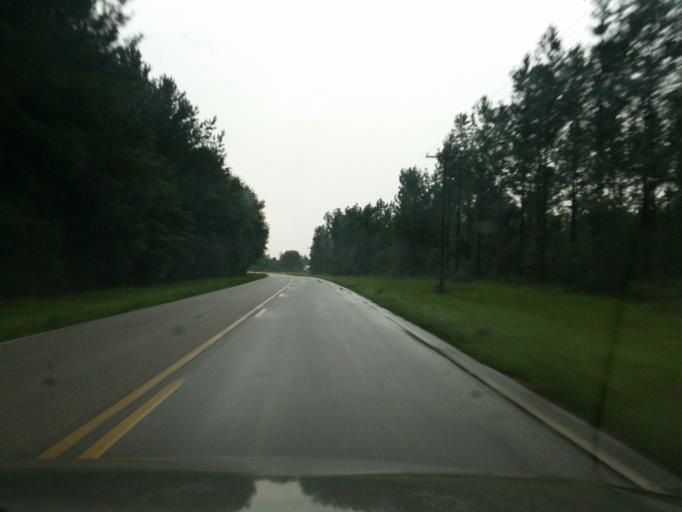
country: US
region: Florida
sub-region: Escambia County
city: Cantonment
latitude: 30.6456
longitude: -87.4475
